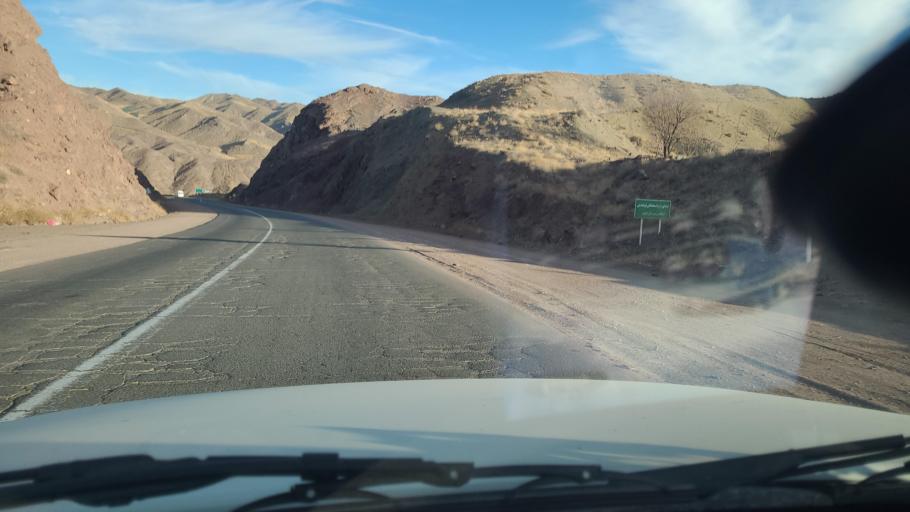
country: IR
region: Razavi Khorasan
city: Sabzevar
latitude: 36.4185
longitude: 57.5607
